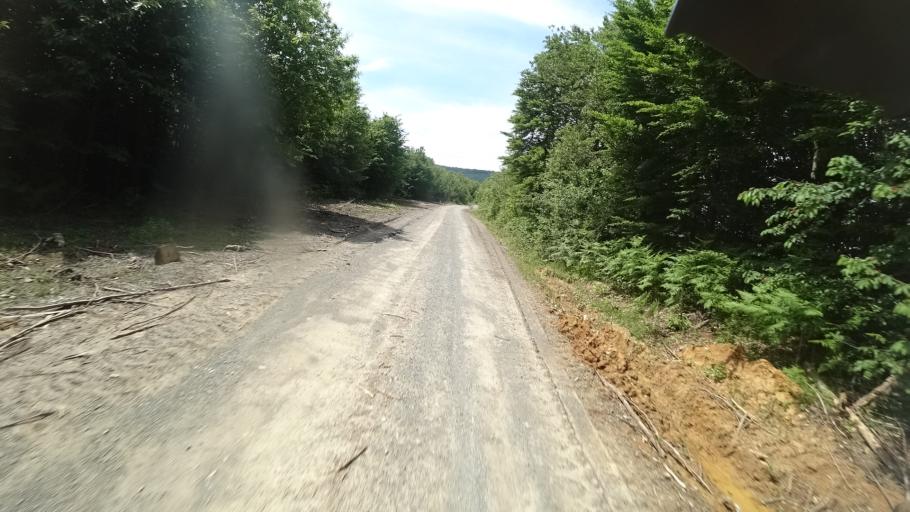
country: HR
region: Sisacko-Moslavacka
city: Gvozd
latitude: 45.3268
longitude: 15.8268
